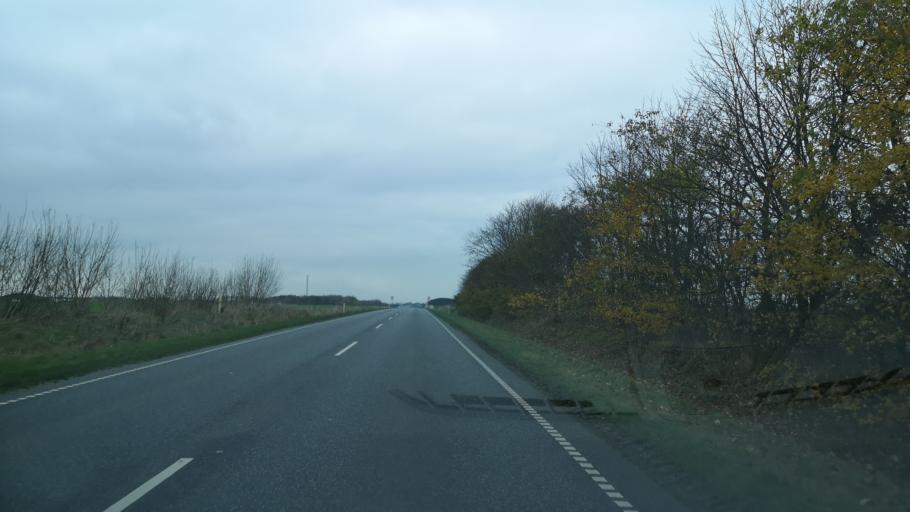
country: DK
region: Central Jutland
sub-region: Ringkobing-Skjern Kommune
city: Videbaek
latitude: 56.0814
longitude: 8.6415
